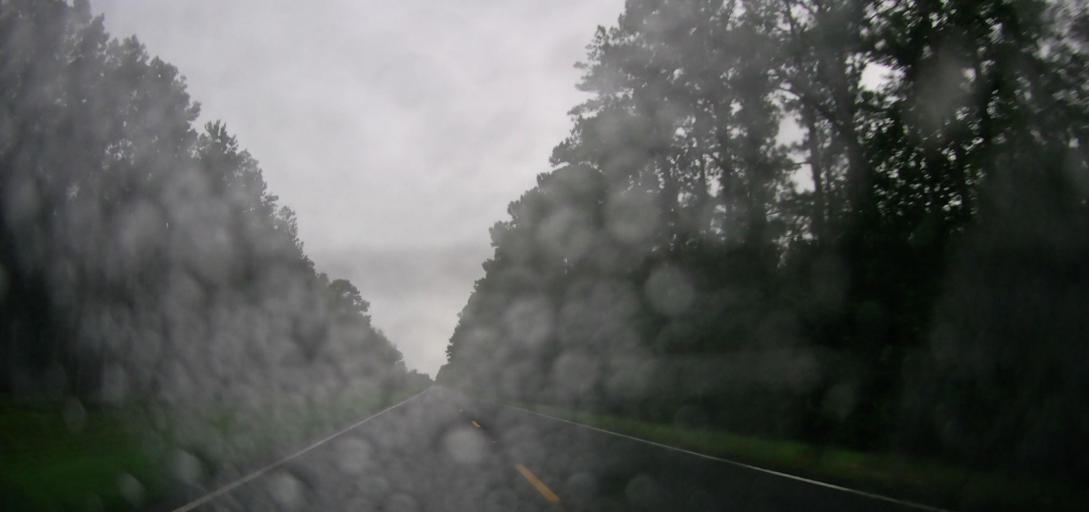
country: US
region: Georgia
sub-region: Glynn County
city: Dock Junction
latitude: 31.2660
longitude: -81.6339
